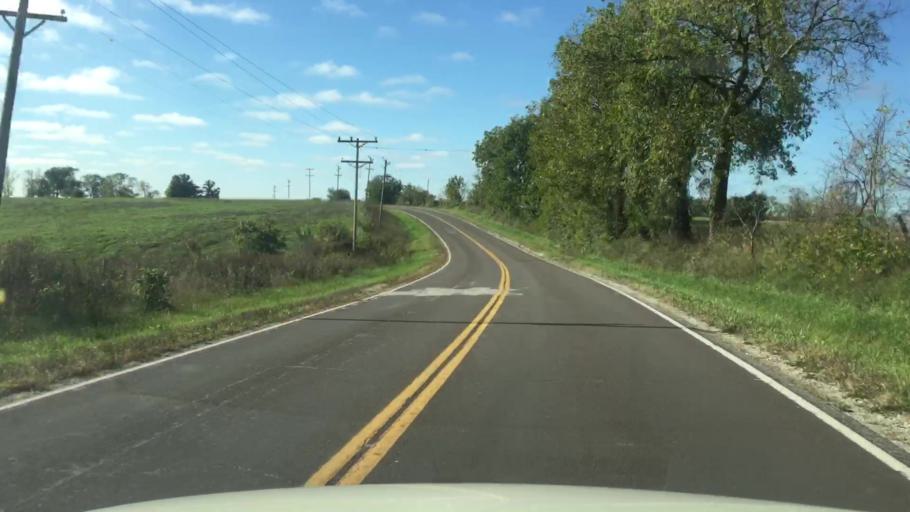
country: US
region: Missouri
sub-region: Howard County
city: New Franklin
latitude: 39.0862
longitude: -92.7452
